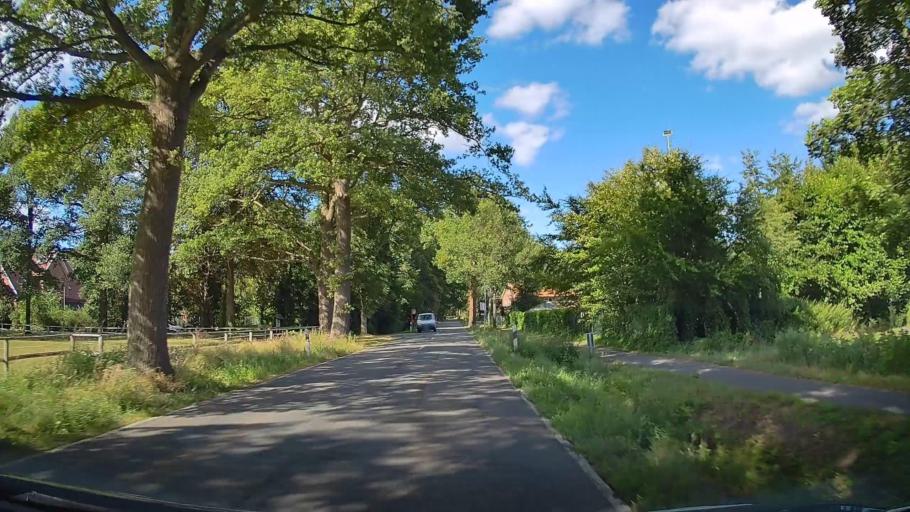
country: DE
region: Lower Saxony
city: Menslage
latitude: 52.6412
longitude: 7.8063
